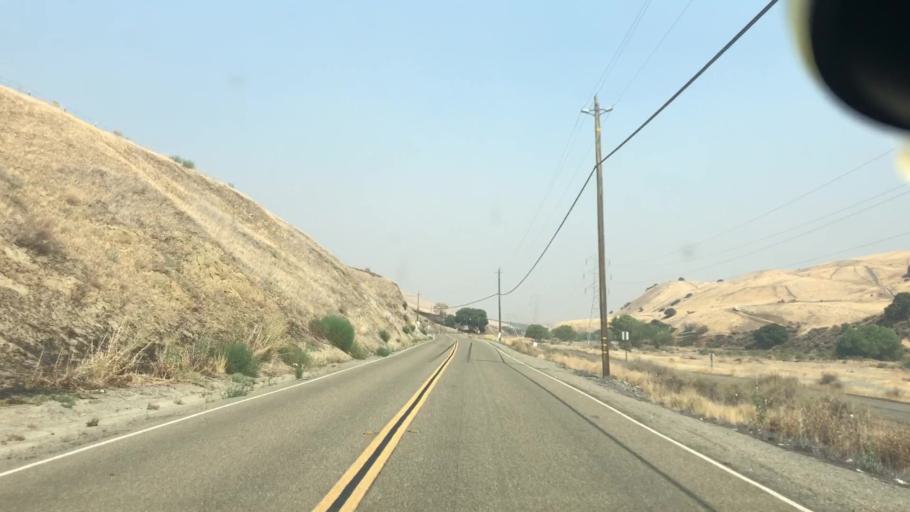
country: US
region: California
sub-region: San Joaquin County
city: Mountain House
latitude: 37.6368
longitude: -121.5626
